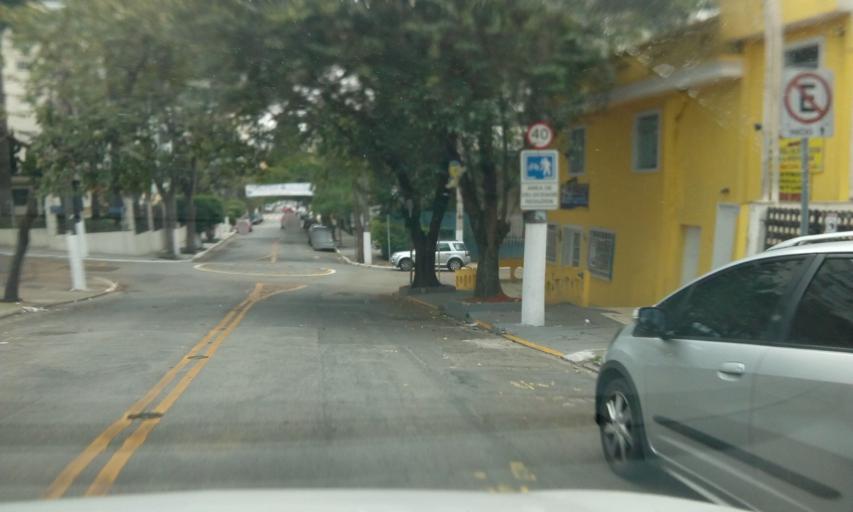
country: BR
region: Sao Paulo
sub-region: Sao Paulo
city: Sao Paulo
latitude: -23.6115
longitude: -46.6570
